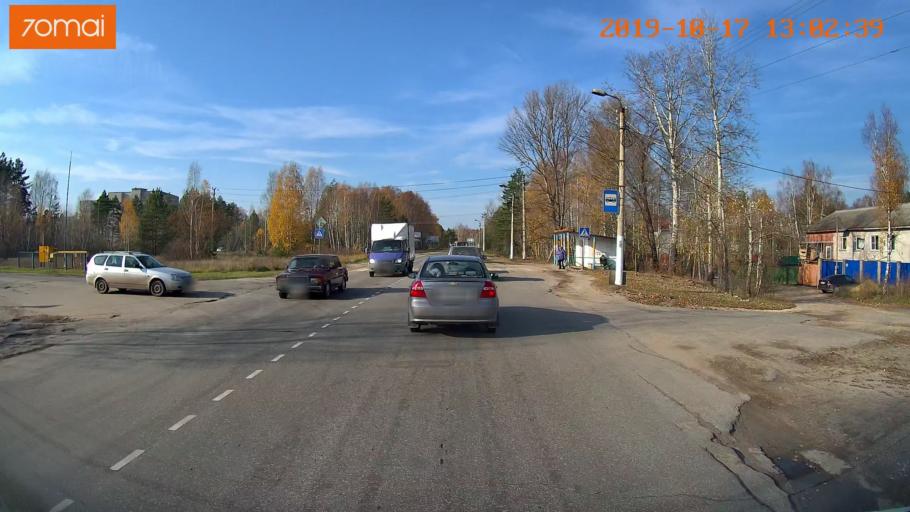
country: RU
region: Rjazan
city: Kasimov
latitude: 54.9507
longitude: 41.3605
